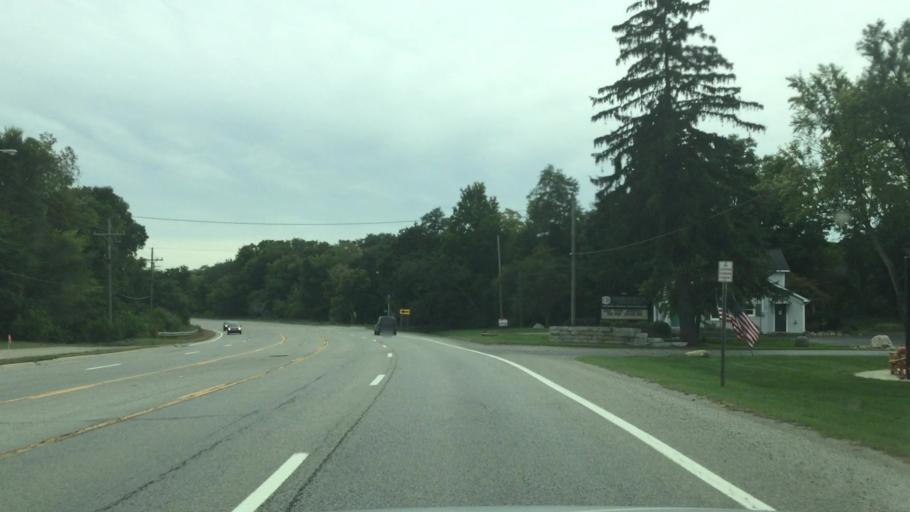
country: US
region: Michigan
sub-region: Oakland County
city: Clarkston
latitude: 42.7528
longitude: -83.4791
